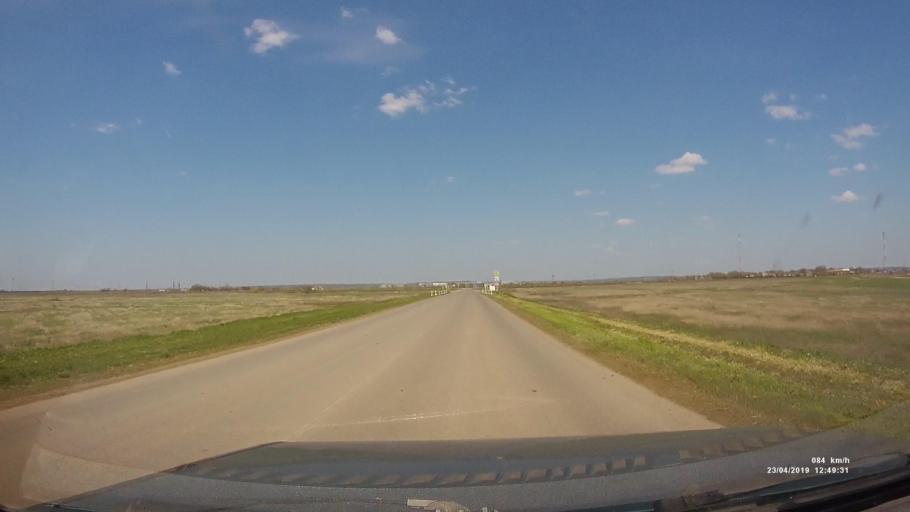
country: RU
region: Kalmykiya
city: Yashalta
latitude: 46.5381
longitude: 42.6396
